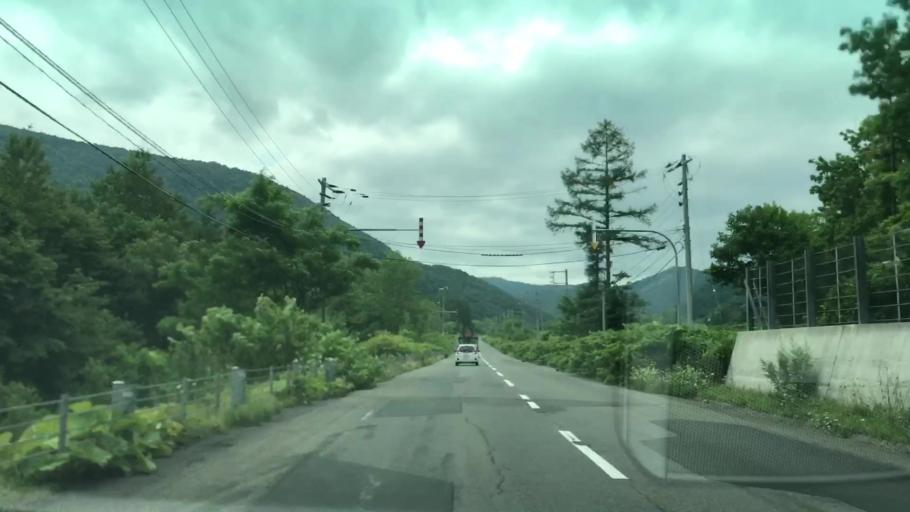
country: JP
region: Hokkaido
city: Yoichi
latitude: 43.0348
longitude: 140.8638
